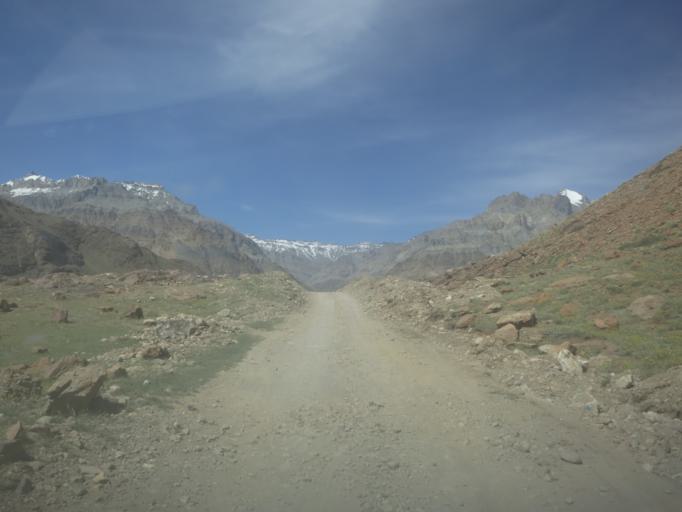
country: IN
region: Himachal Pradesh
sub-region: Kulu
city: Manali
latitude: 32.4349
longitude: 77.6777
